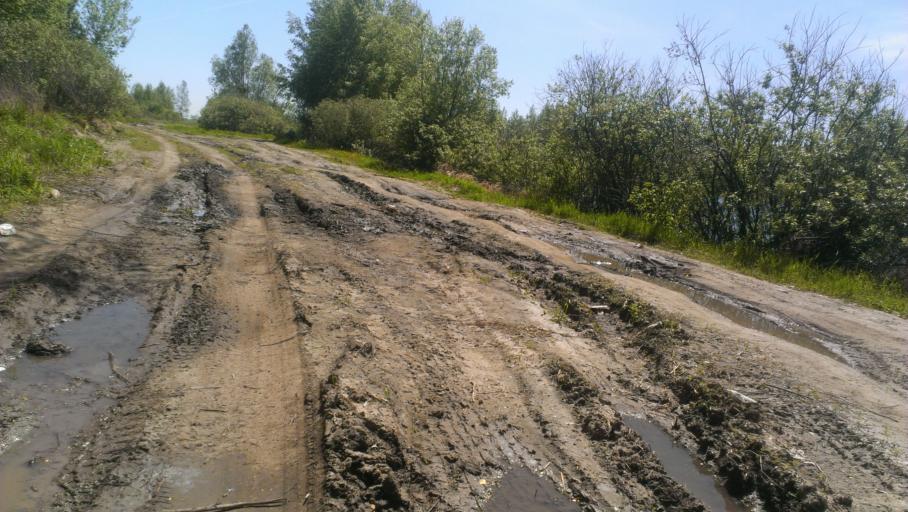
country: RU
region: Altai Krai
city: Zaton
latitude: 53.3143
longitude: 83.8510
